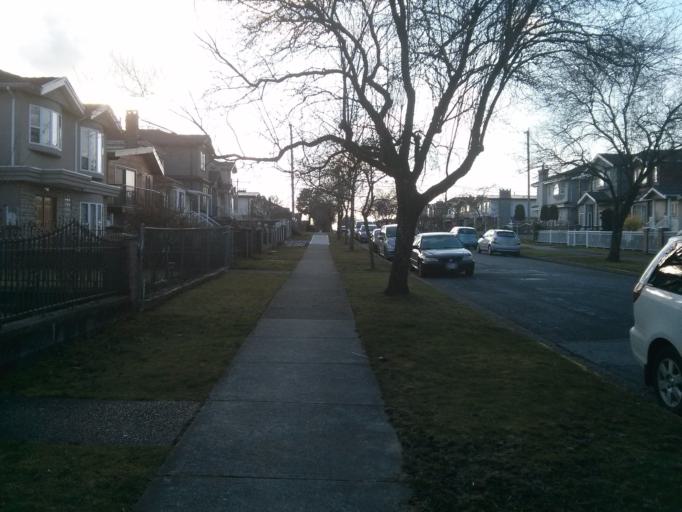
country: CA
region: British Columbia
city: Burnaby
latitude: 49.2479
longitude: -123.0275
